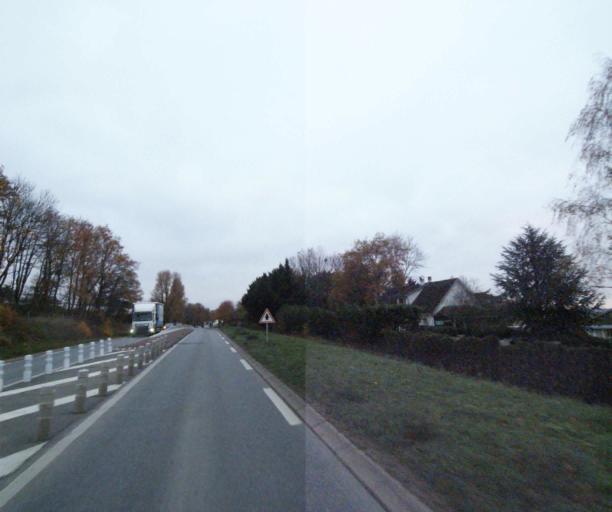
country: FR
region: Ile-de-France
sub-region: Departement des Yvelines
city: Villennes-sur-Seine
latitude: 48.9489
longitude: 1.9794
